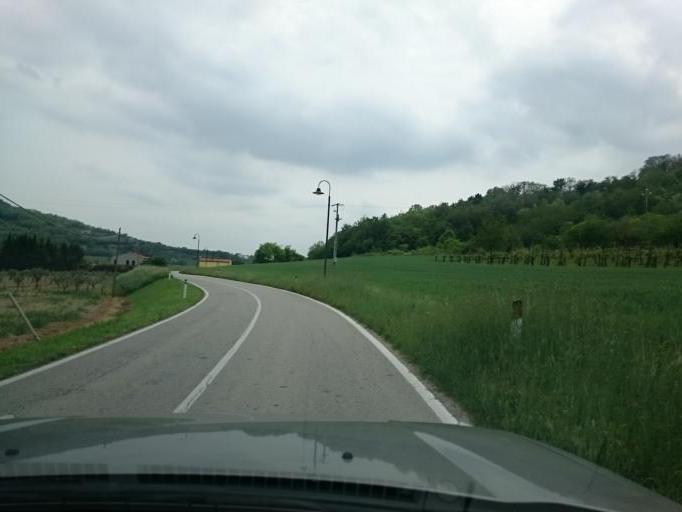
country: IT
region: Veneto
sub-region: Provincia di Padova
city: Arqua Petrarca
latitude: 45.2643
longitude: 11.7202
